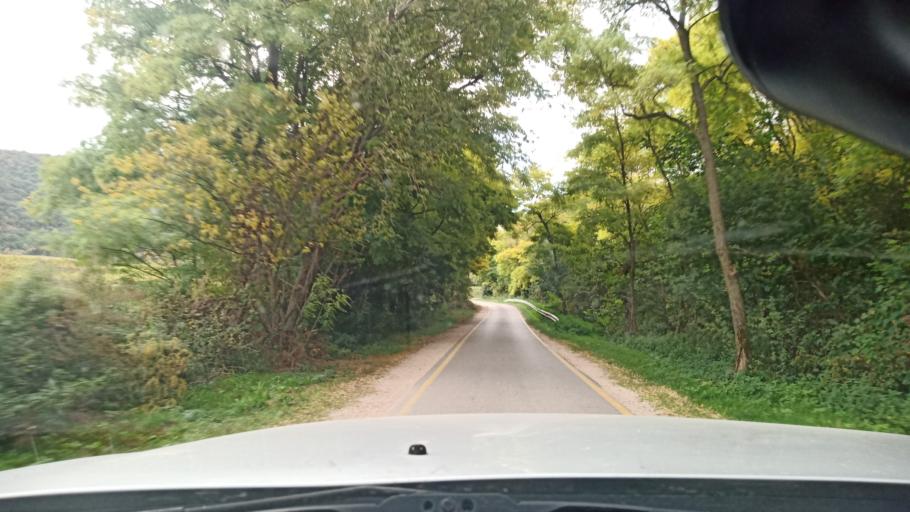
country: HU
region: Fejer
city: Mor
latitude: 47.3734
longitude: 18.2353
